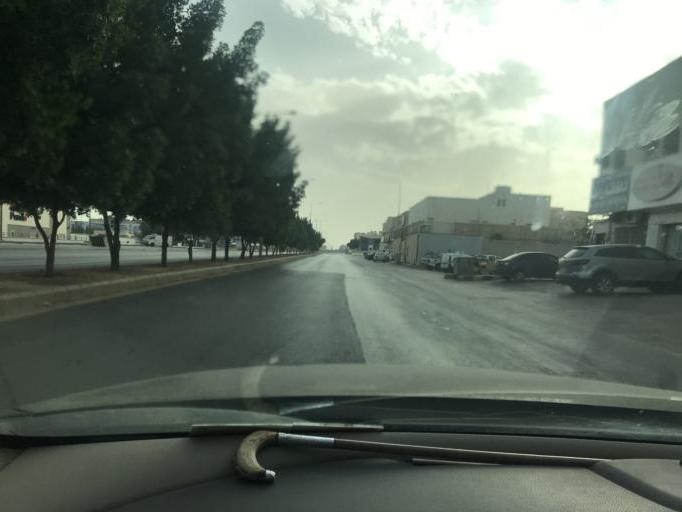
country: SA
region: Ar Riyad
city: Riyadh
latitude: 24.7787
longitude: 46.7107
